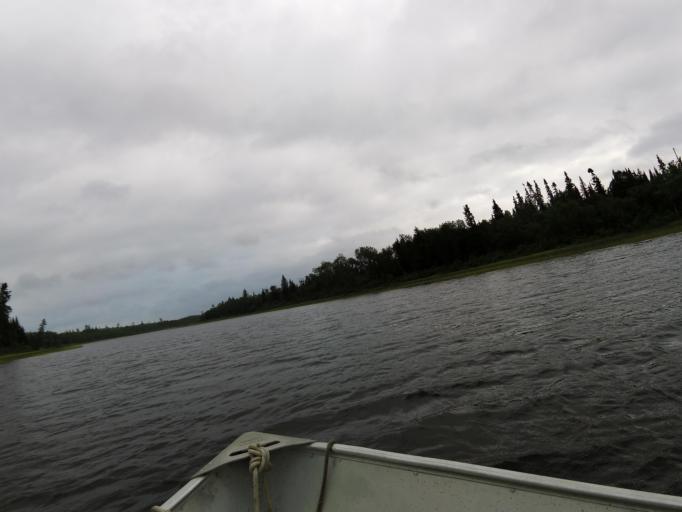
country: CA
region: Ontario
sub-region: Rainy River District
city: Atikokan
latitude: 49.5931
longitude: -91.3589
